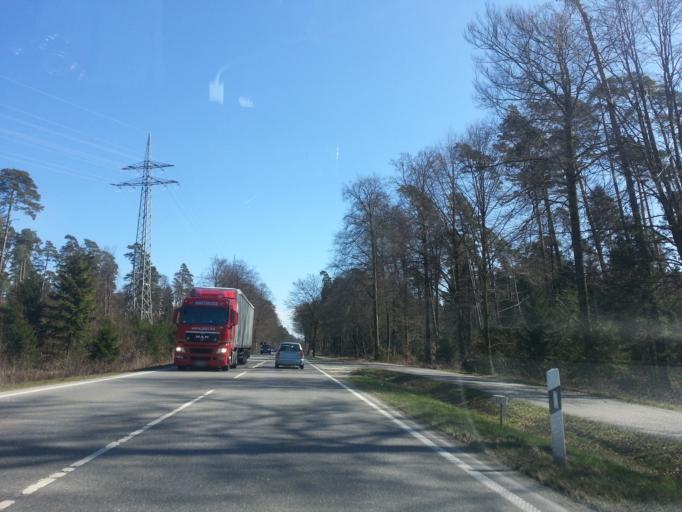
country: DE
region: Baden-Wuerttemberg
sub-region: Tuebingen Region
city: Eriskirch
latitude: 47.6267
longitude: 9.5481
